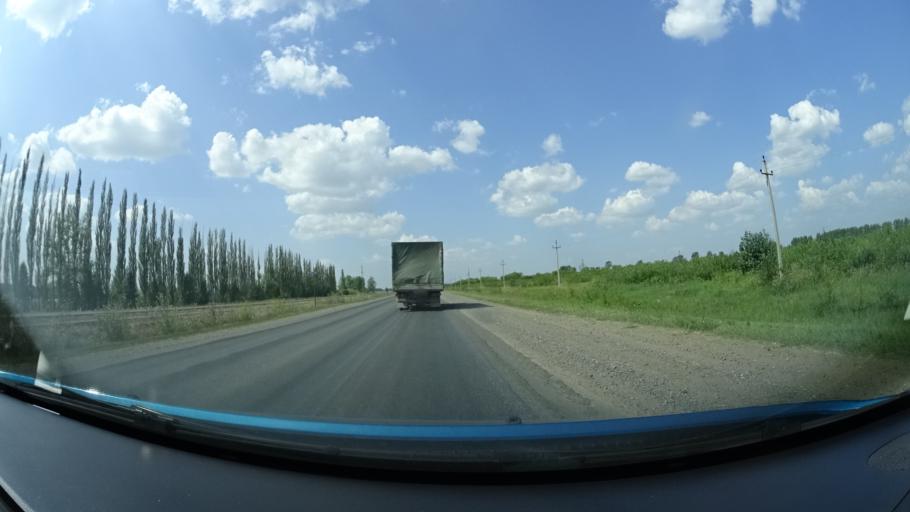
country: RU
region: Bashkortostan
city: Buzdyak
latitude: 54.6422
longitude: 54.5221
